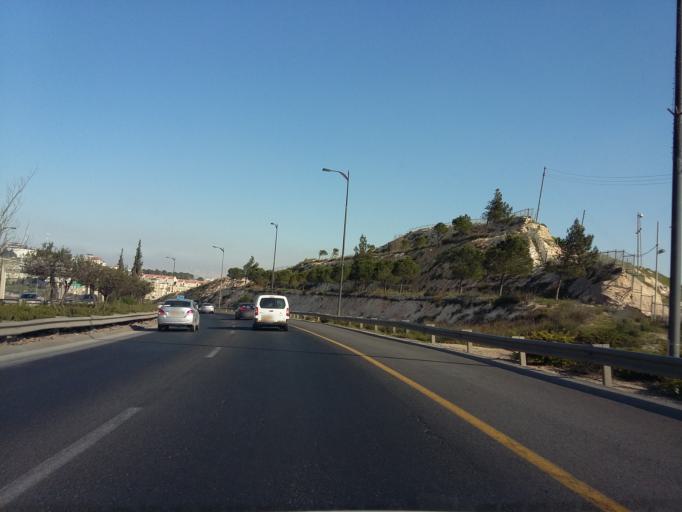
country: PS
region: West Bank
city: `Anata
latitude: 31.8138
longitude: 35.2387
